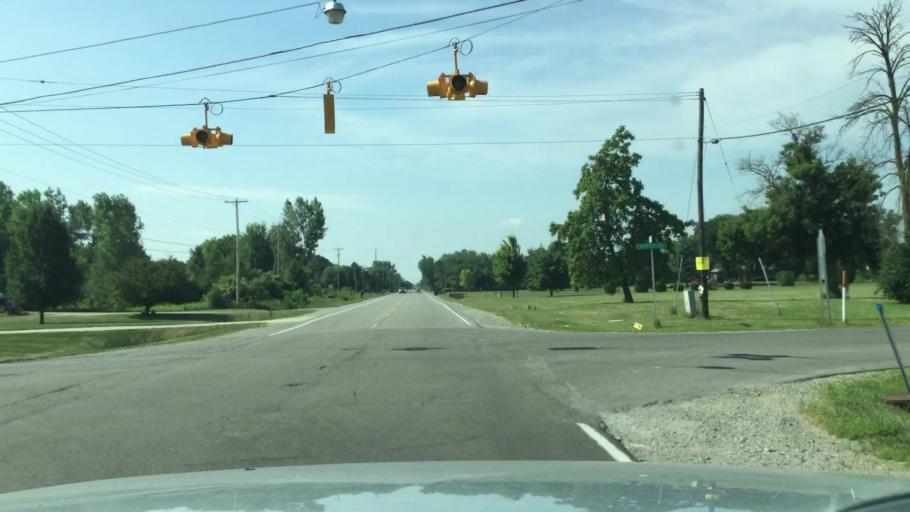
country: US
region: Michigan
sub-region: Genesee County
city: Flushing
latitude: 43.0785
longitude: -83.8134
